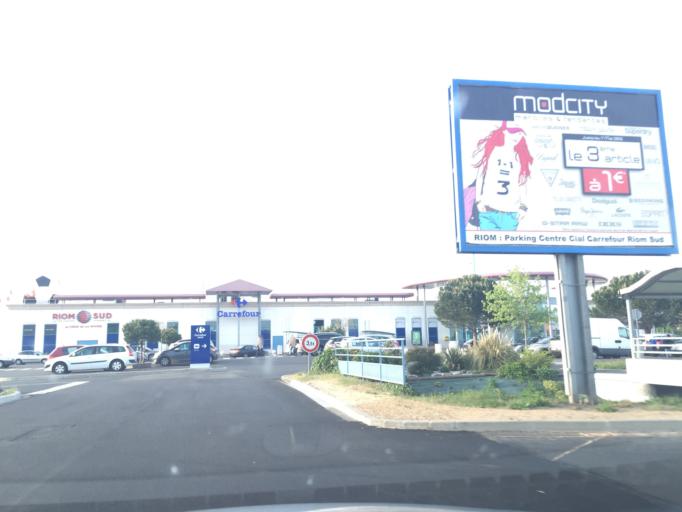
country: FR
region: Auvergne
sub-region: Departement du Puy-de-Dome
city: Menetrol
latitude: 45.8750
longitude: 3.1188
